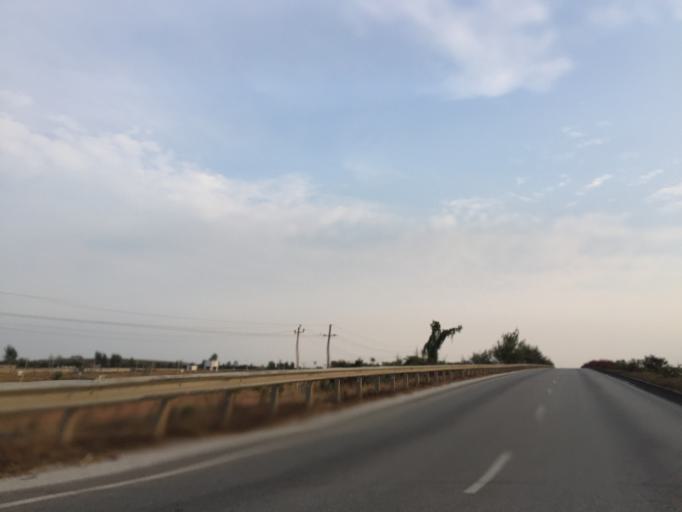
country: IN
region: Karnataka
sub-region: Chikkaballapur
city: Chik Ballapur
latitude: 13.4087
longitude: 77.7431
